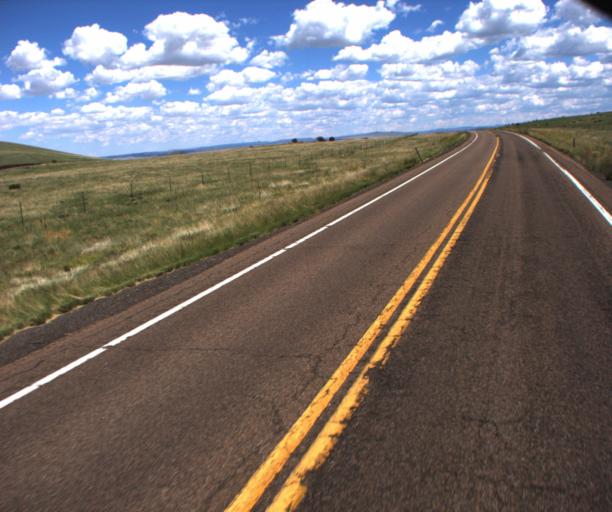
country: US
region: Arizona
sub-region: Apache County
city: Springerville
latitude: 34.2206
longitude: -109.4807
